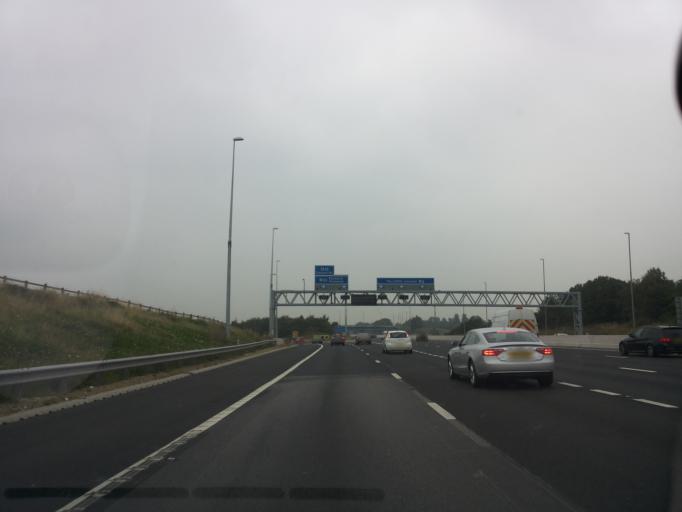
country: GB
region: England
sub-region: Lancashire
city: Goosnargh
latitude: 53.8045
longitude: -2.6955
